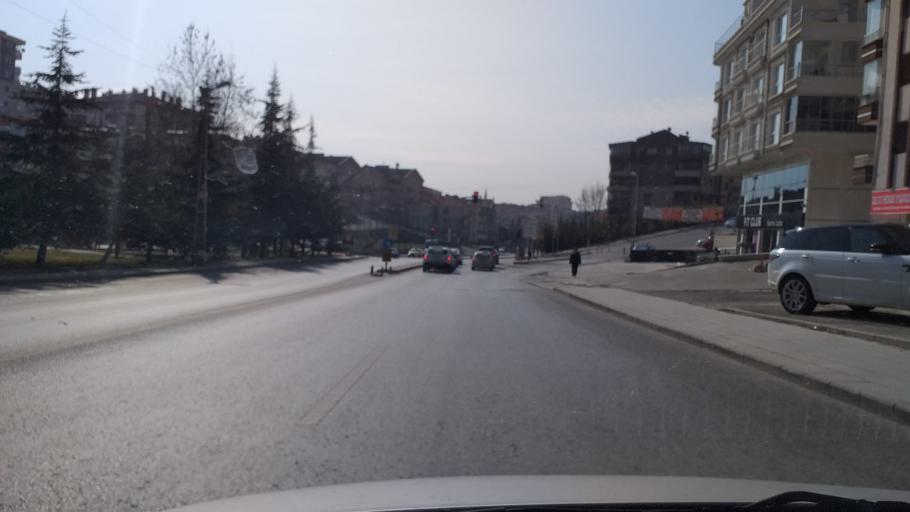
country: TR
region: Ankara
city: Ankara
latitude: 39.9926
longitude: 32.8564
